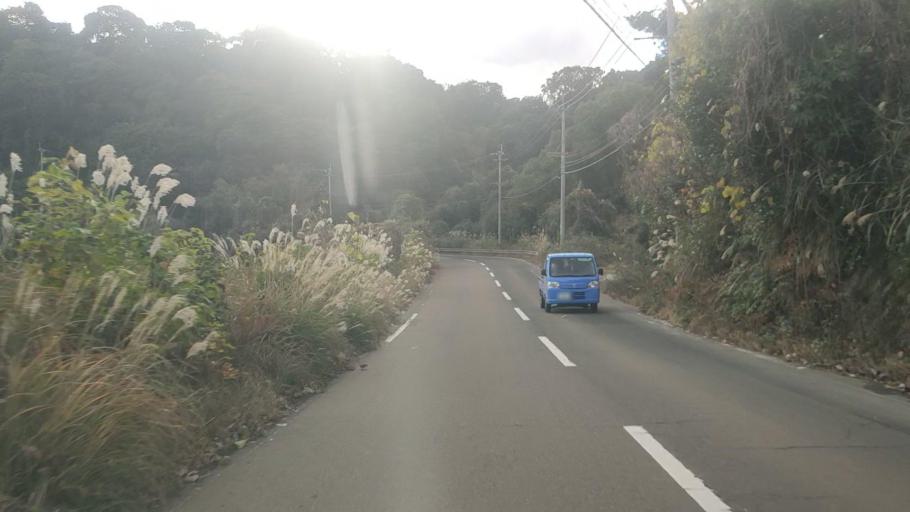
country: JP
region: Kagoshima
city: Hamanoichi
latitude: 31.6188
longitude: 130.6746
